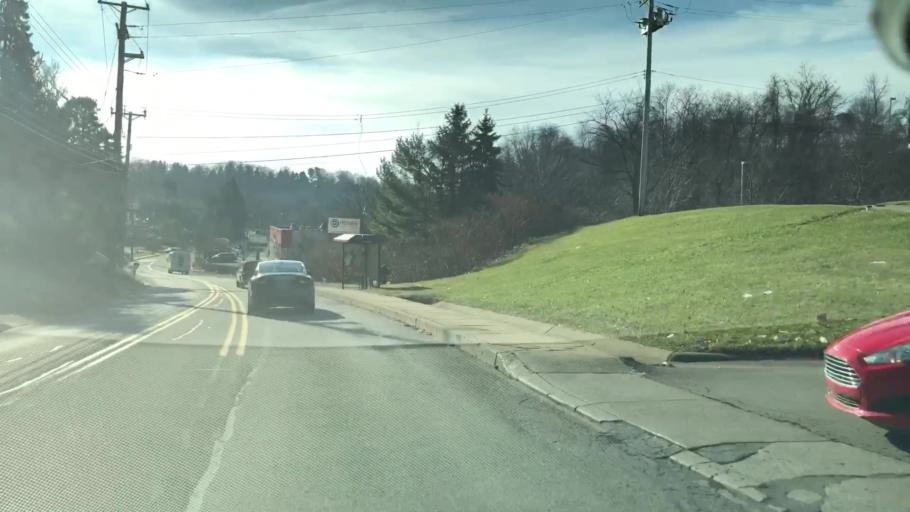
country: US
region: Pennsylvania
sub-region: Allegheny County
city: Churchill
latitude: 40.4611
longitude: -79.8240
